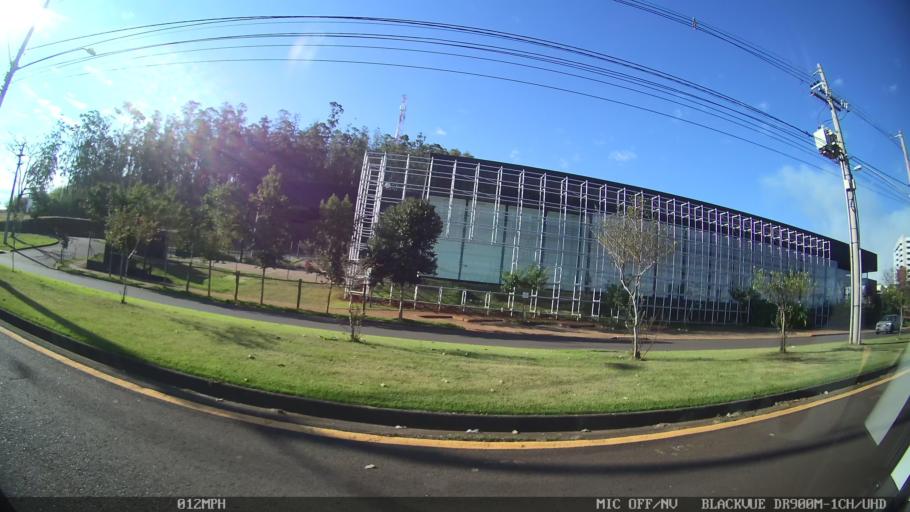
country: BR
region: Sao Paulo
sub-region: Piracicaba
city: Piracicaba
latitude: -22.6944
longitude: -47.6232
